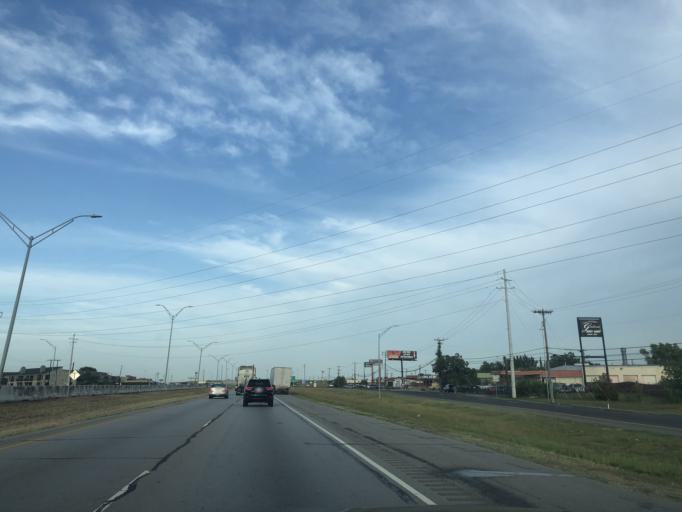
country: US
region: Texas
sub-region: Dallas County
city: Mesquite
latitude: 32.7923
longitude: -96.6398
